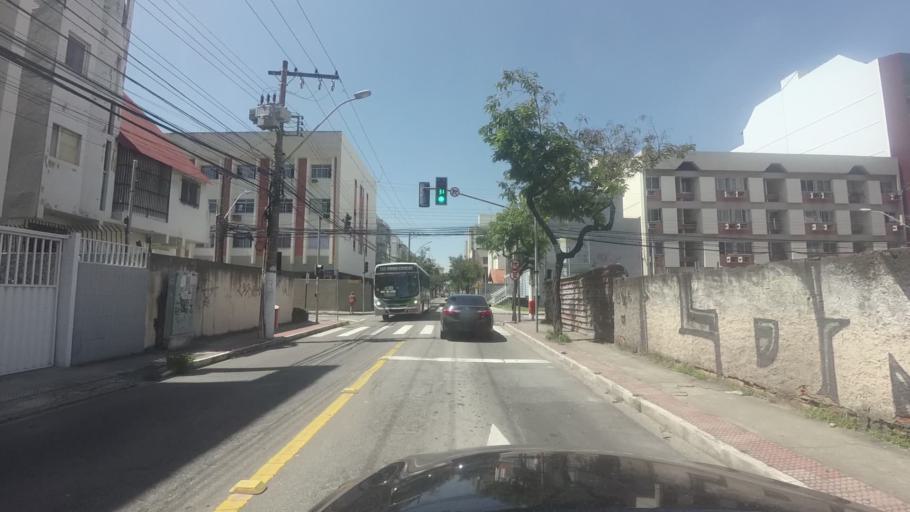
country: BR
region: Espirito Santo
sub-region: Vila Velha
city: Vila Velha
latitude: -20.2627
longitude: -40.2637
